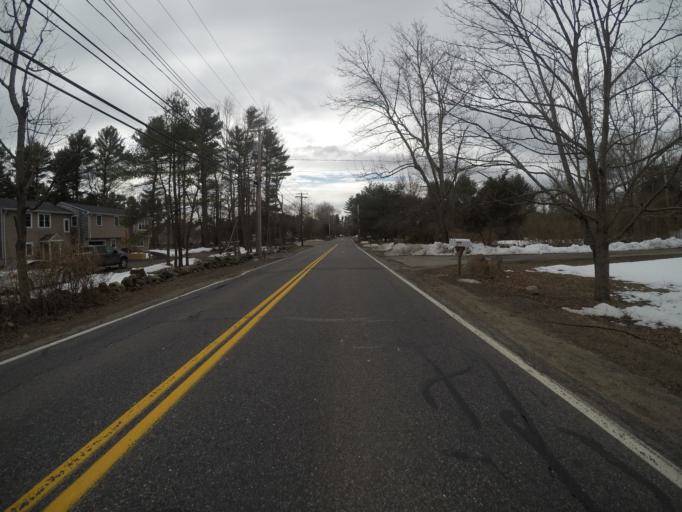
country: US
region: Massachusetts
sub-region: Bristol County
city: Easton
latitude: 42.0626
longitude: -71.1330
